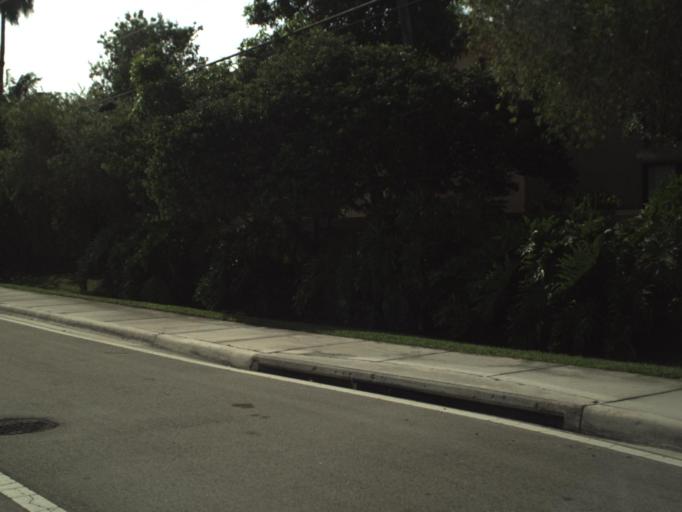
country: US
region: Florida
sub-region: Broward County
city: Coral Springs
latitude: 26.2728
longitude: -80.2757
